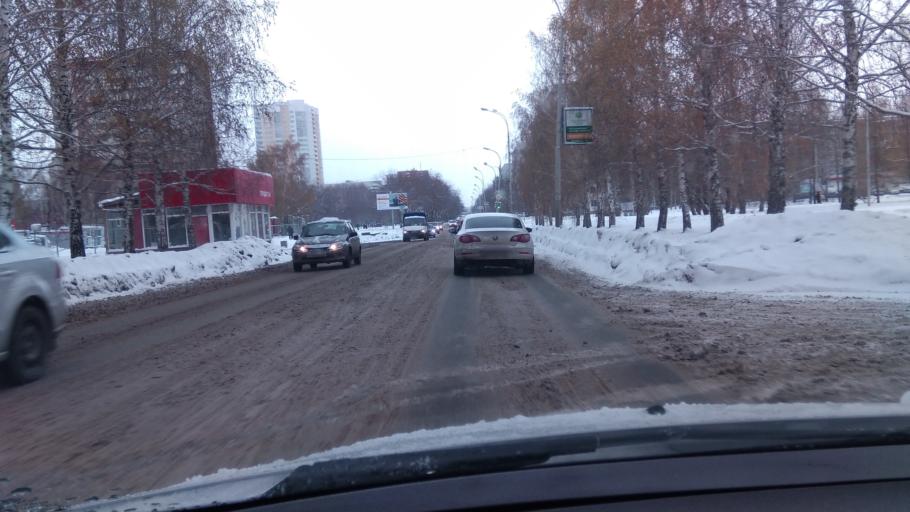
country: RU
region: Sverdlovsk
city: Sovkhoznyy
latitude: 56.8138
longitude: 60.5724
